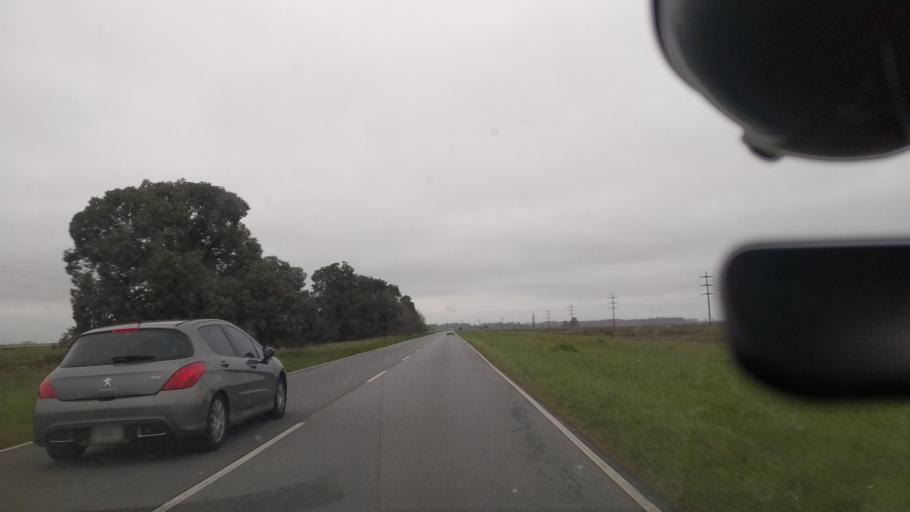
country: AR
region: Buenos Aires
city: Veronica
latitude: -35.3600
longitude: -57.4024
